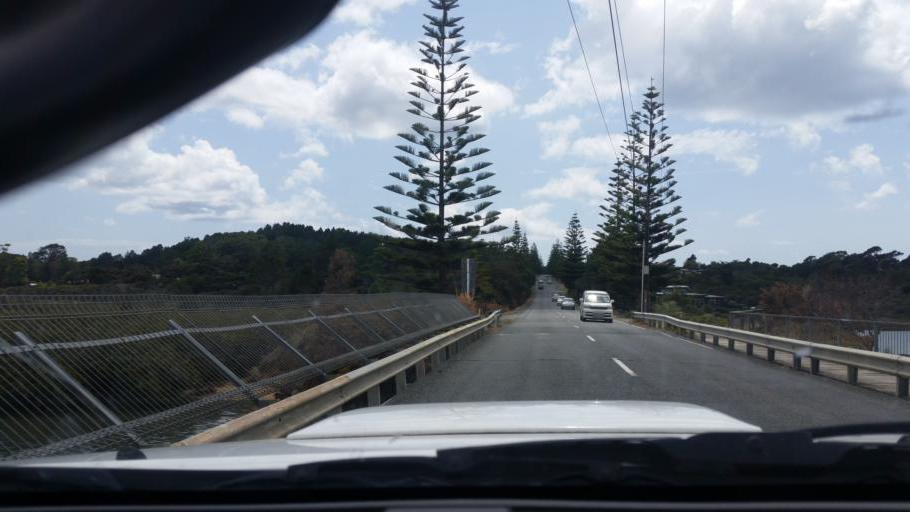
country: NZ
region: Auckland
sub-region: Auckland
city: Wellsford
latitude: -36.1087
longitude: 174.5793
